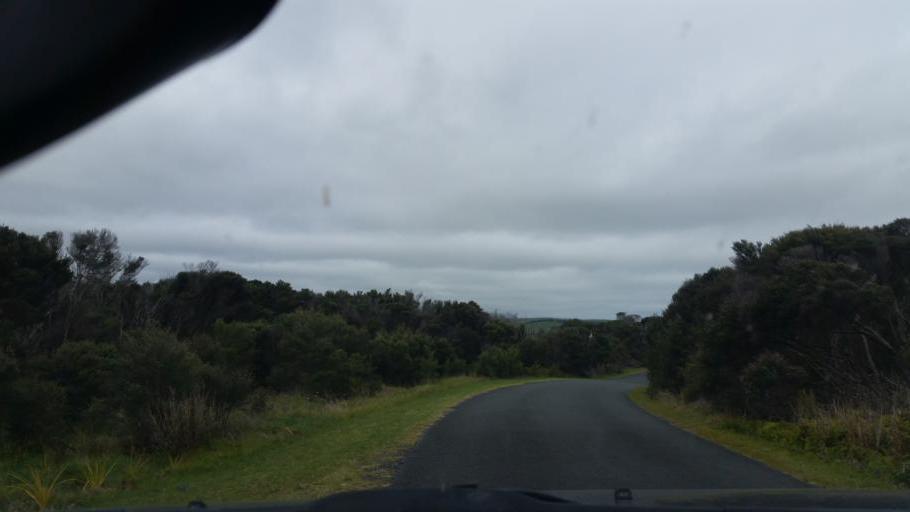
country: NZ
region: Northland
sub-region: Kaipara District
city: Dargaville
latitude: -35.8124
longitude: 173.6515
